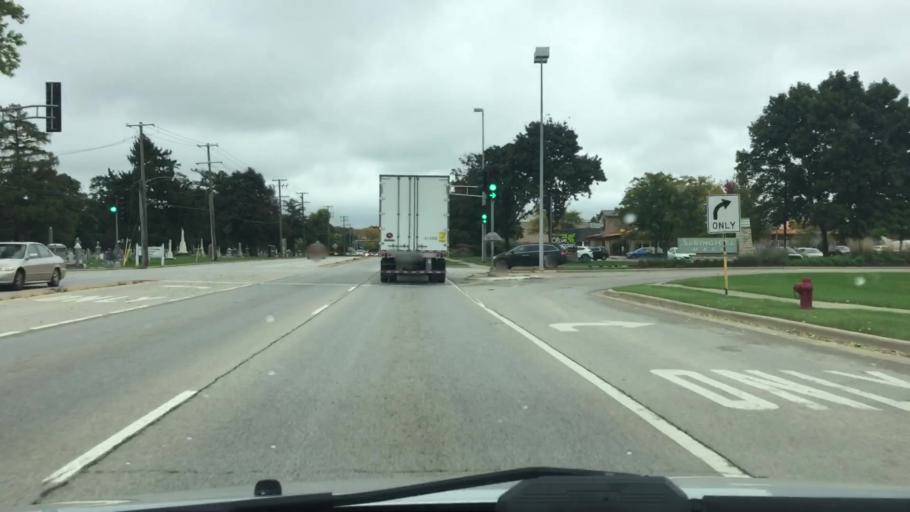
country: US
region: Illinois
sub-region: Kane County
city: West Dundee
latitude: 42.1039
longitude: -88.2904
